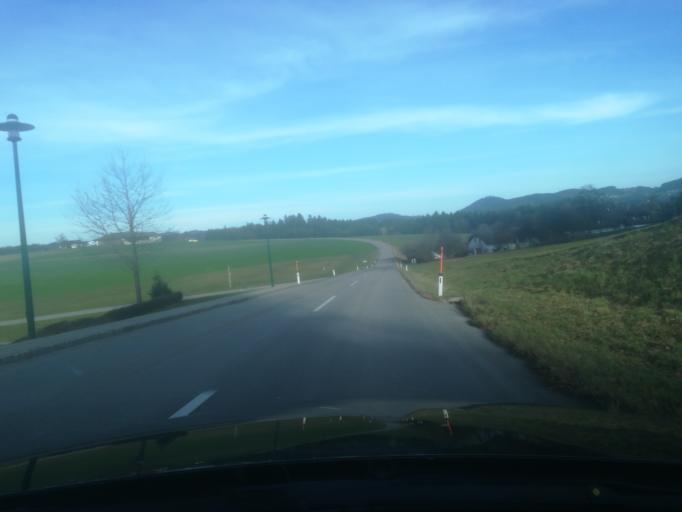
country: AT
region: Upper Austria
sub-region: Politischer Bezirk Perg
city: Perg
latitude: 48.3074
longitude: 14.6597
